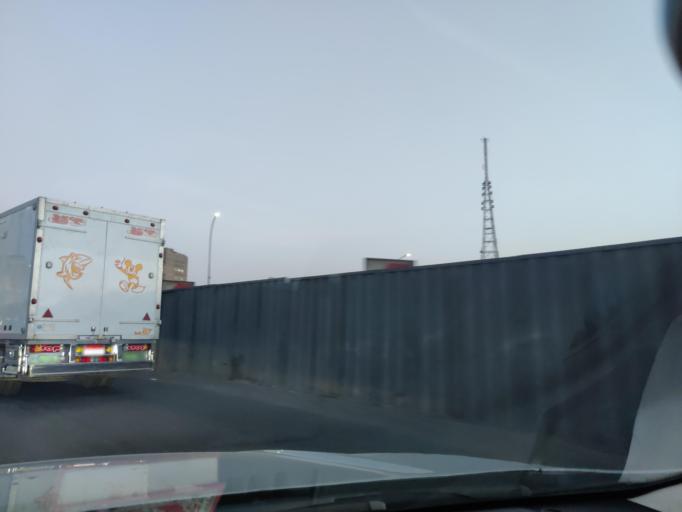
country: EG
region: Muhafazat al Qahirah
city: Cairo
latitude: 30.1001
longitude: 31.3052
